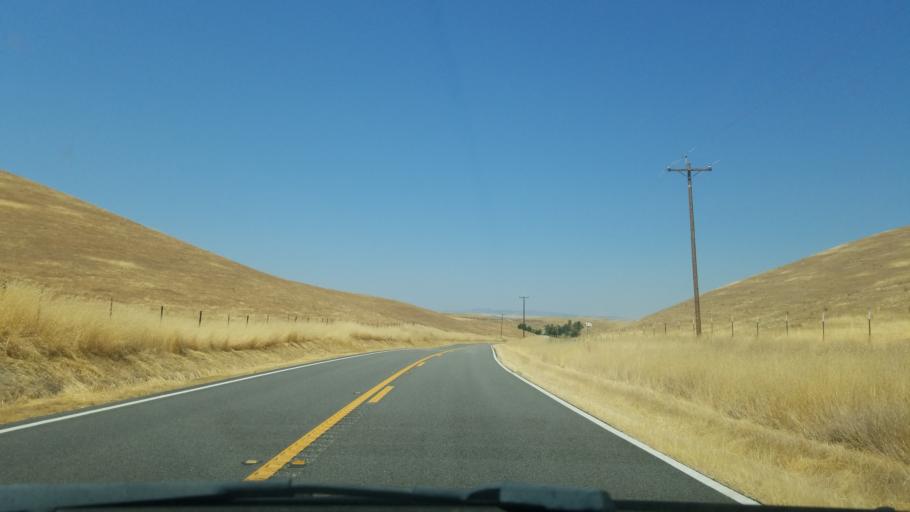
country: US
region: California
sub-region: San Luis Obispo County
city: Shandon
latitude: 35.6091
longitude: -120.4071
